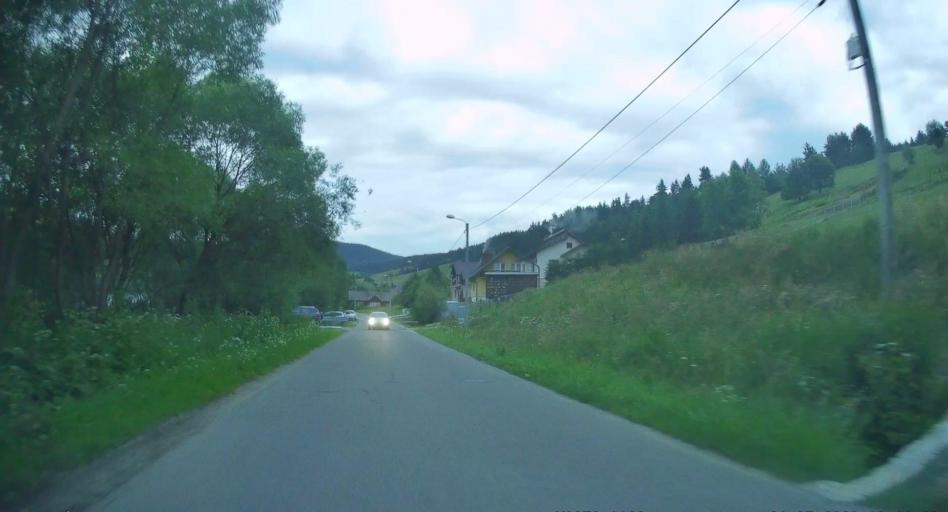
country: PL
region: Lesser Poland Voivodeship
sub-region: Powiat nowosadecki
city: Muszyna
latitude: 49.3785
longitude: 20.9236
